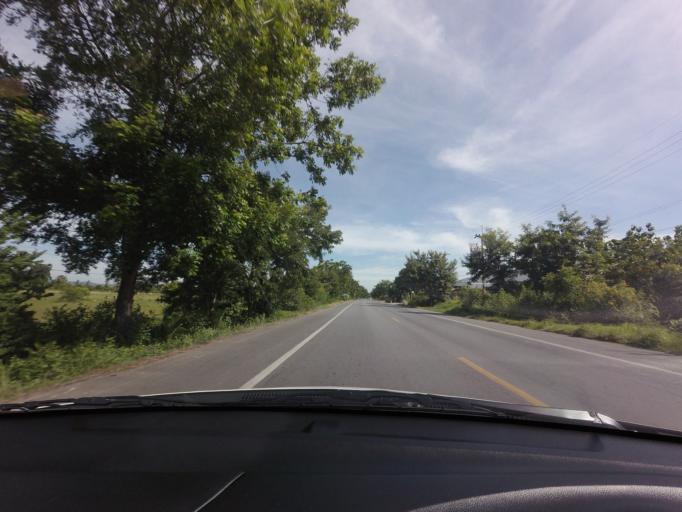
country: TH
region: Kanchanaburi
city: Lao Khwan
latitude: 14.5443
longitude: 99.9047
